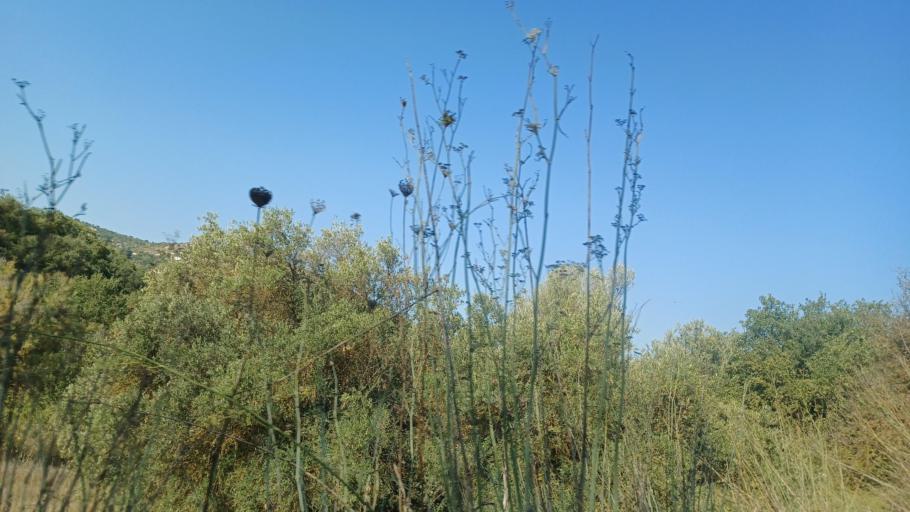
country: CY
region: Pafos
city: Polis
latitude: 34.9435
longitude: 32.4741
